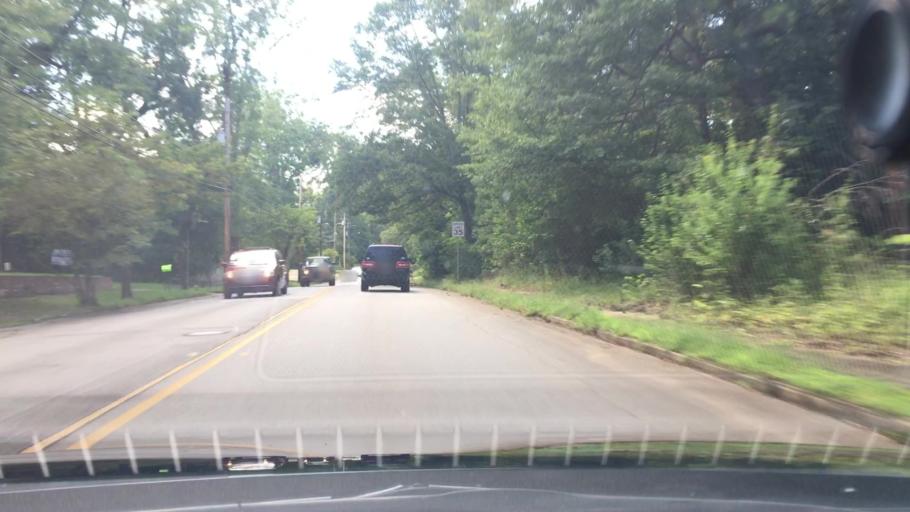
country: US
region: Georgia
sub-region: Jasper County
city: Monticello
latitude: 33.3000
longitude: -83.6755
